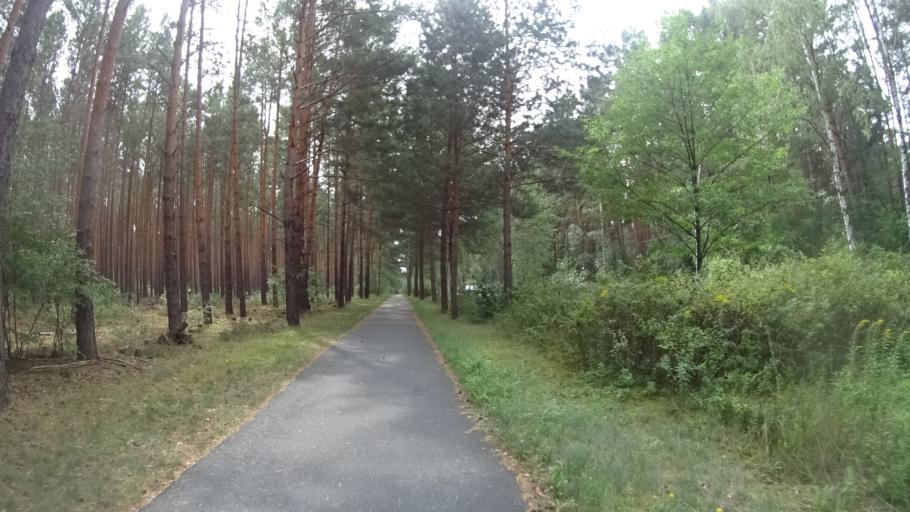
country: DE
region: Brandenburg
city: Borkwalde
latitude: 52.2660
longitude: 12.8348
